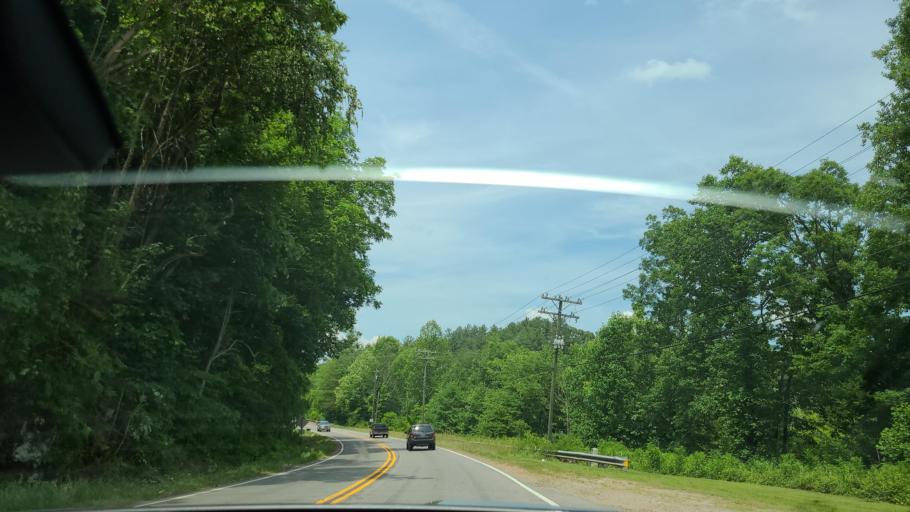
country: US
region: North Carolina
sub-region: Macon County
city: Franklin
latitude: 35.1660
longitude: -83.3203
